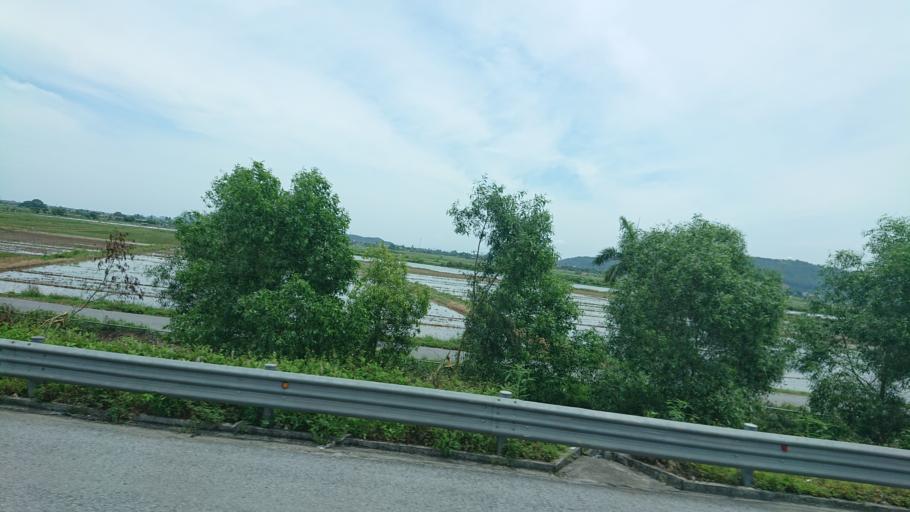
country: VN
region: Hai Phong
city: Tien Lang
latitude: 20.7708
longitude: 106.6013
